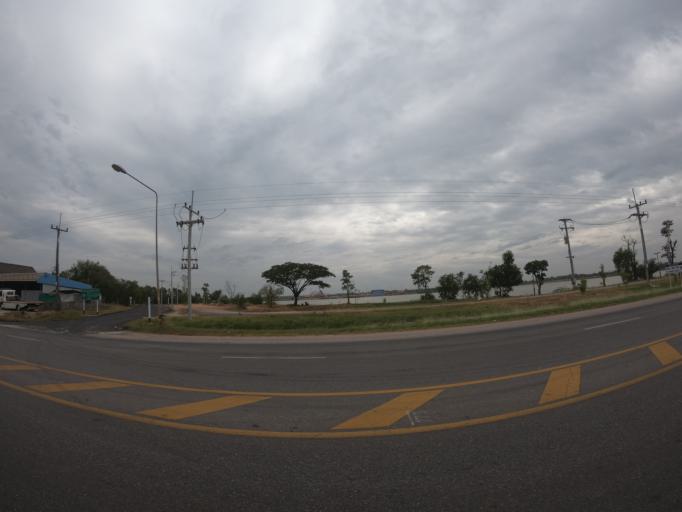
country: TH
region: Roi Et
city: Thawat Buri
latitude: 16.0828
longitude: 103.7218
